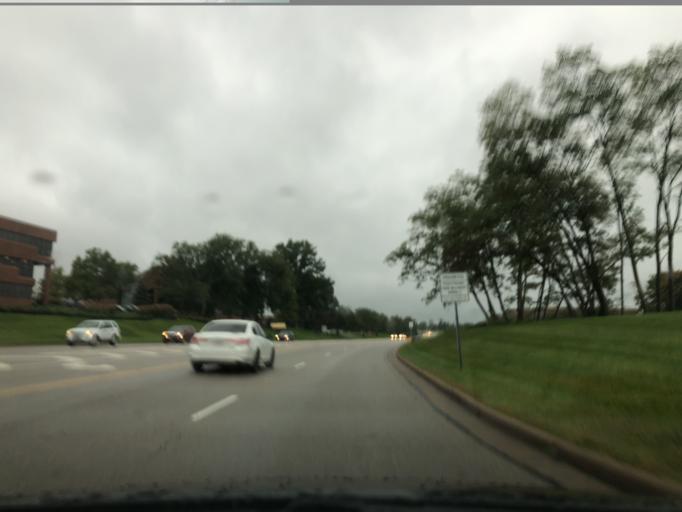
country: US
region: Ohio
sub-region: Hamilton County
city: Blue Ash
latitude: 39.2458
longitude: -84.3815
